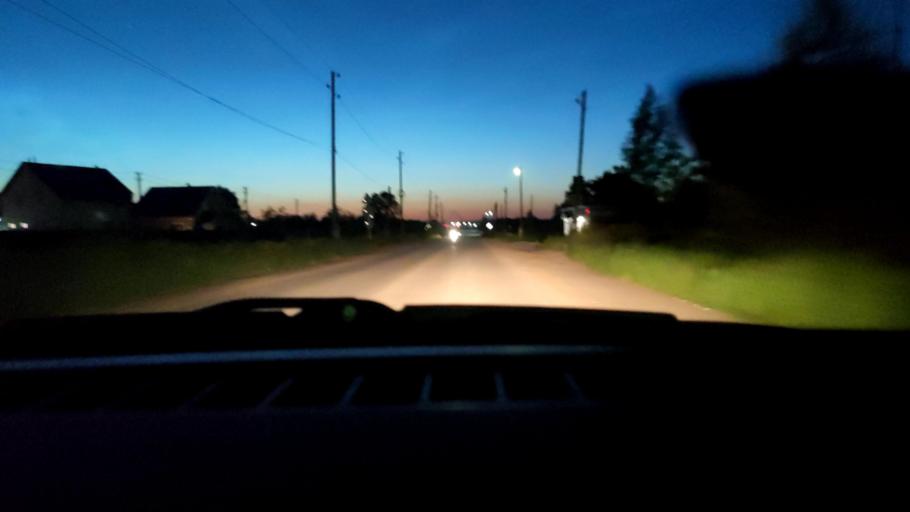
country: RU
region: Perm
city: Kultayevo
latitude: 57.8716
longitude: 55.9181
